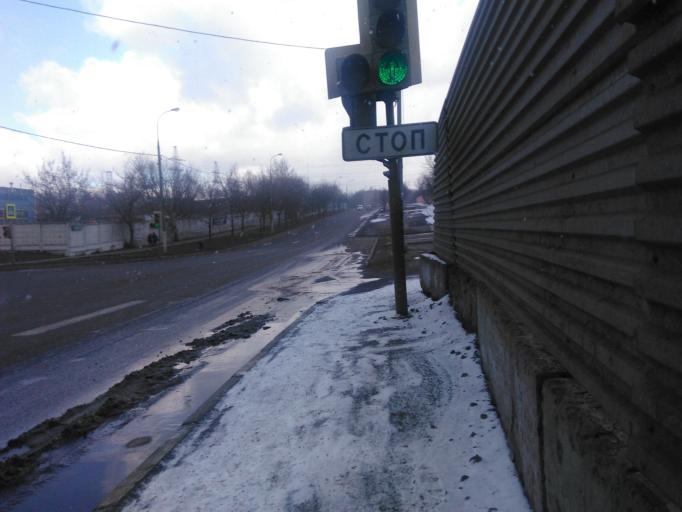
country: RU
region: Moscow
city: Tsaritsyno
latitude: 55.6451
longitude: 37.6425
